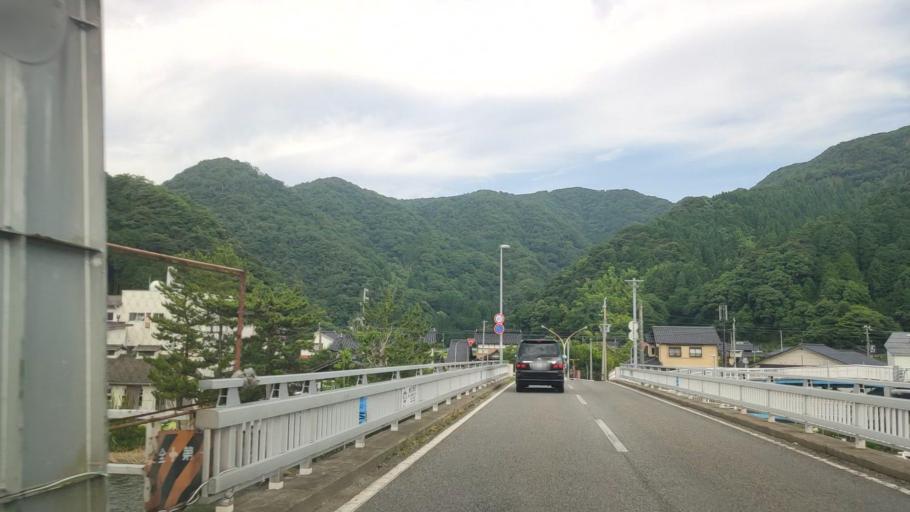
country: JP
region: Hyogo
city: Toyooka
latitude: 35.6419
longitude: 134.8252
